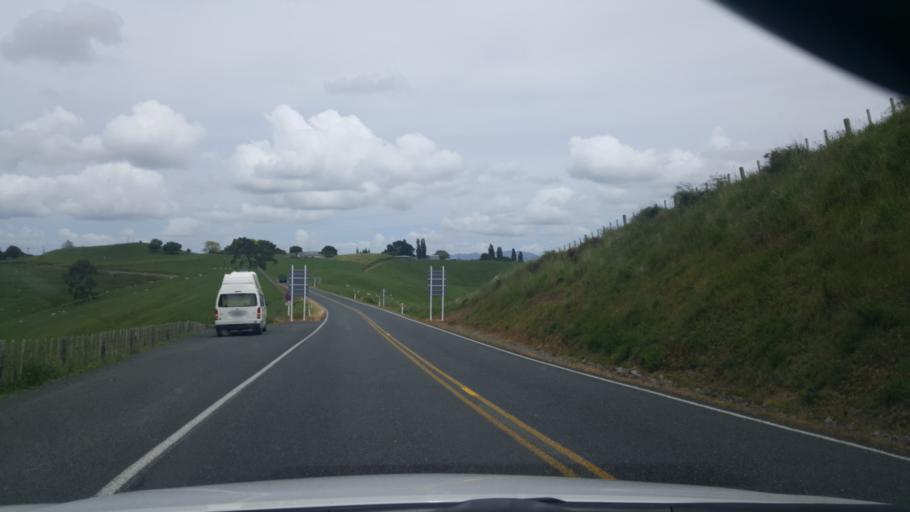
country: NZ
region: Waikato
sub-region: Matamata-Piako District
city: Matamata
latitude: -37.8726
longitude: 175.6861
